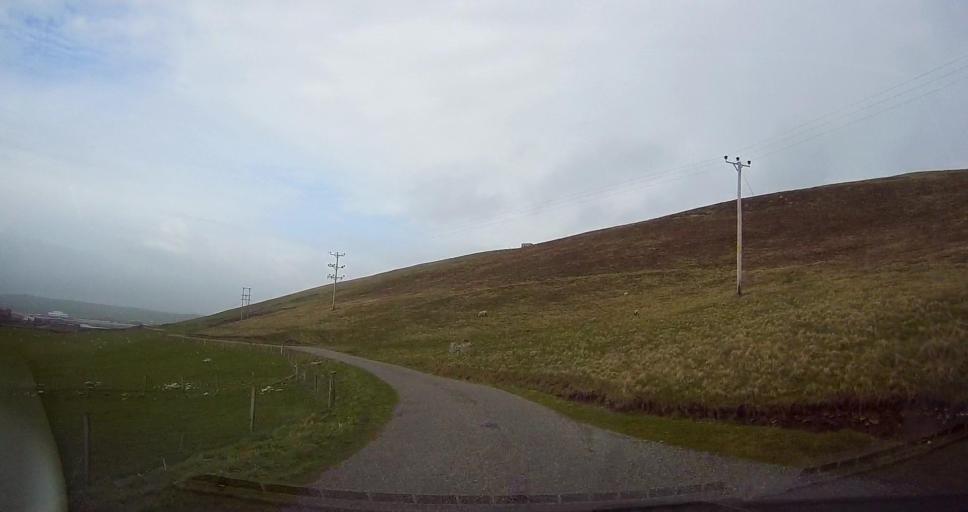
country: GB
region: Scotland
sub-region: Shetland Islands
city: Sandwick
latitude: 59.8633
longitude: -1.2776
